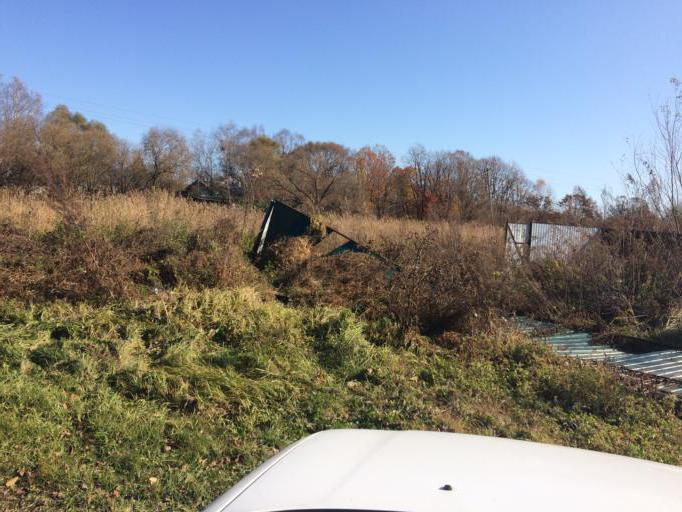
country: RU
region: Primorskiy
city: Dal'nerechensk
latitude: 45.9119
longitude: 133.8050
